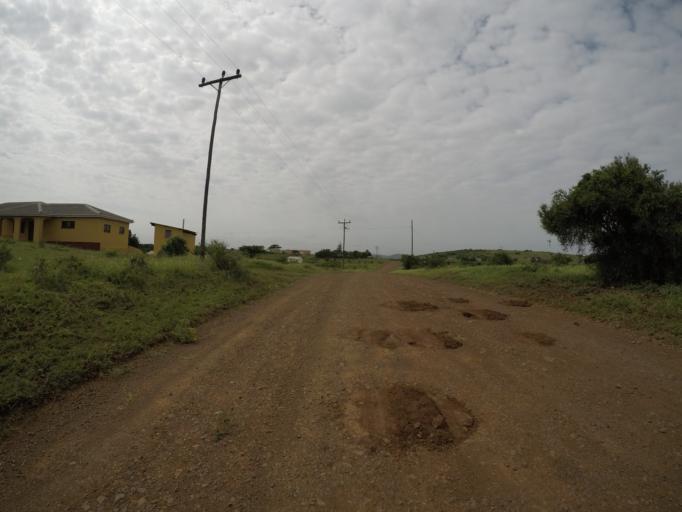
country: ZA
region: KwaZulu-Natal
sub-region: uThungulu District Municipality
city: Empangeni
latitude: -28.6172
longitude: 31.9023
